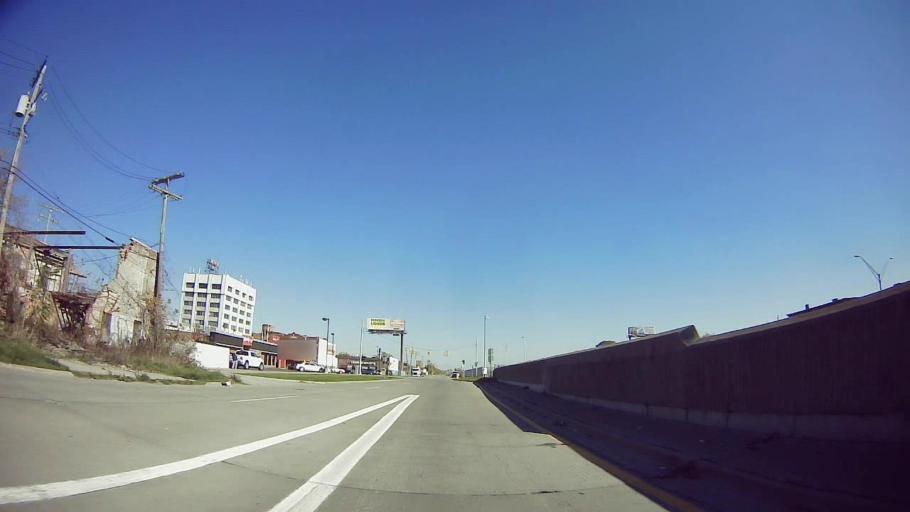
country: US
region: Michigan
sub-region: Wayne County
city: Highland Park
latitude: 42.4032
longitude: -83.0970
